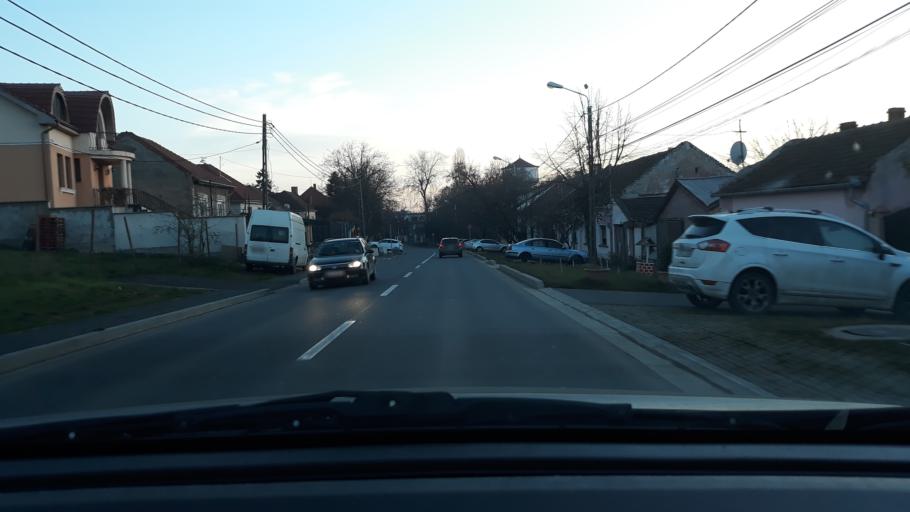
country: RO
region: Bihor
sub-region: Comuna Biharea
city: Oradea
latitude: 47.0843
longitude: 21.9272
